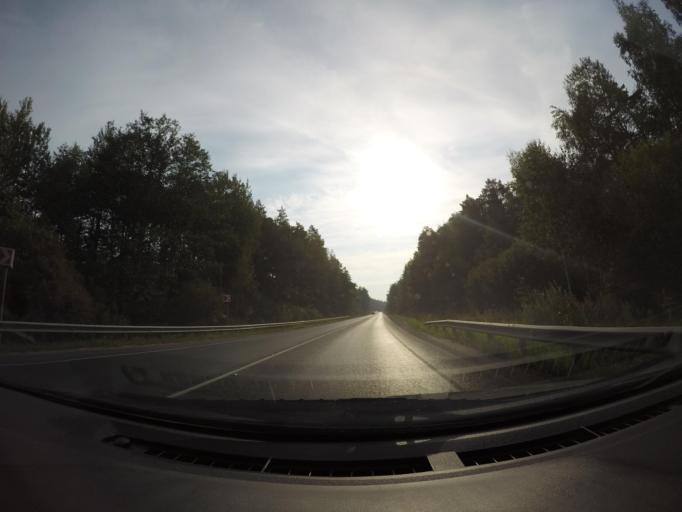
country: RU
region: Moskovskaya
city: Ramenskoye
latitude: 55.6393
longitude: 38.2411
